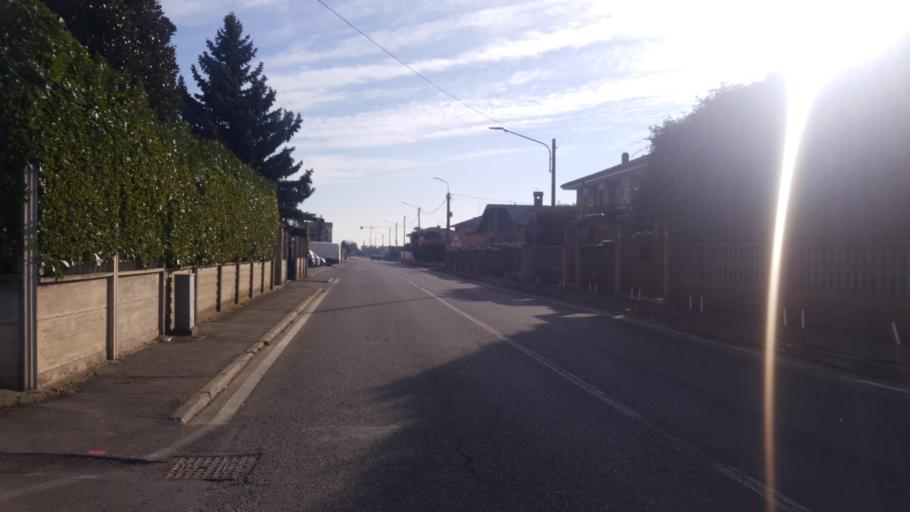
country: IT
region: Lombardy
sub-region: Provincia di Como
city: Turate
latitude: 45.6585
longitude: 9.0123
